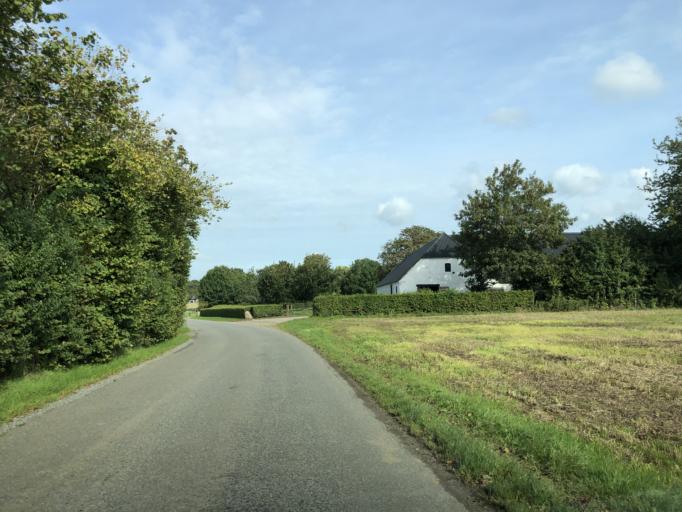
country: DK
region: South Denmark
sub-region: Vejle Kommune
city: Borkop
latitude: 55.6122
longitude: 9.6723
